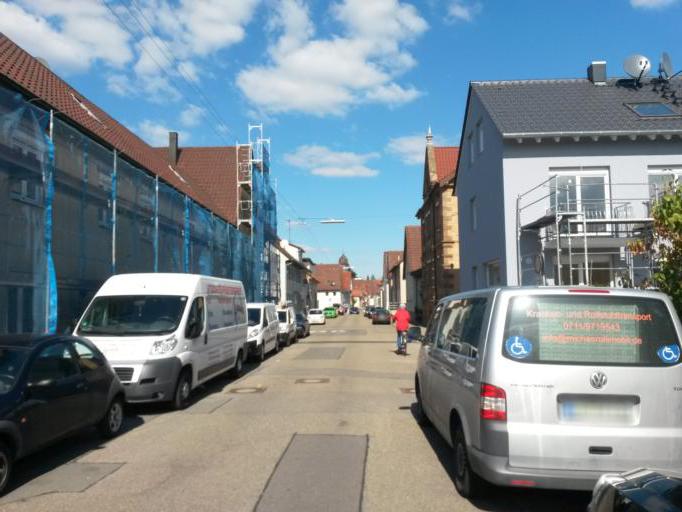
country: DE
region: Baden-Wuerttemberg
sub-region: Karlsruhe Region
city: Muhlacker
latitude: 48.9366
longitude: 8.8397
